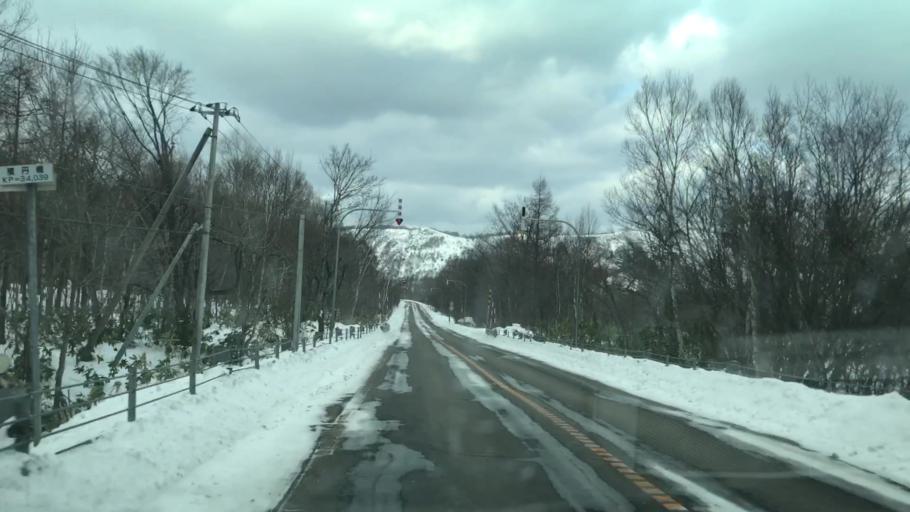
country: JP
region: Hokkaido
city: Yoichi
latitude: 43.3251
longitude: 140.5023
